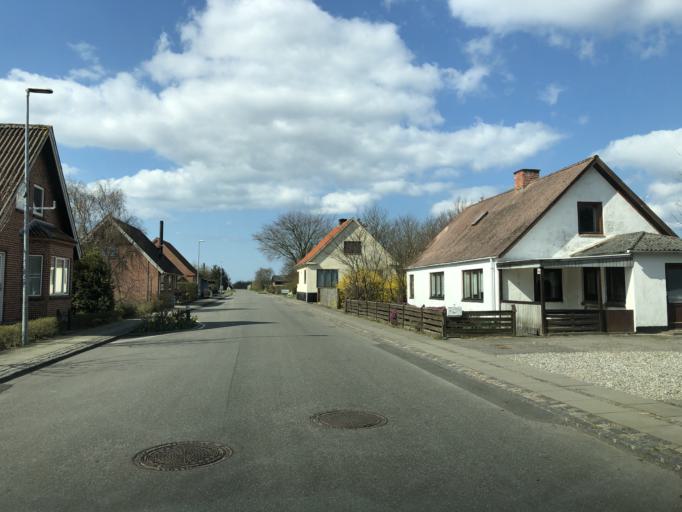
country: DK
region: Central Jutland
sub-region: Holstebro Kommune
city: Ulfborg
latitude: 56.3947
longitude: 8.2118
